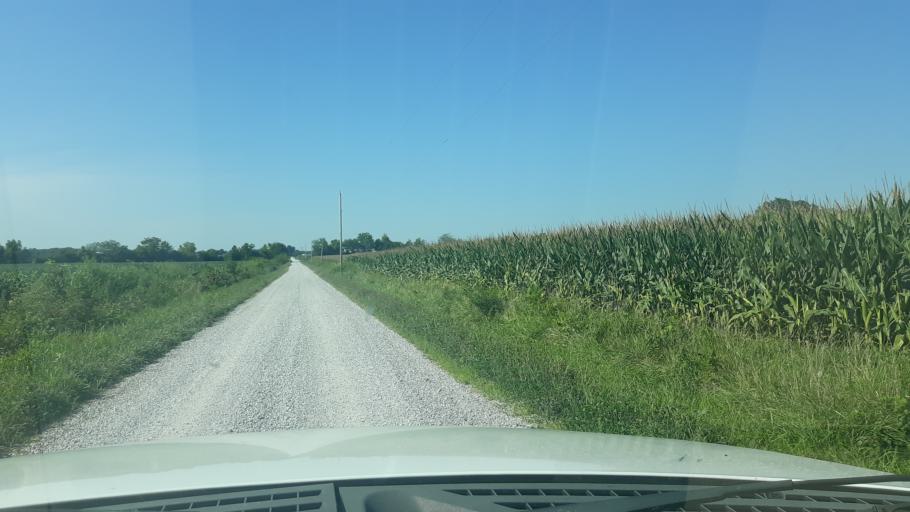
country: US
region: Illinois
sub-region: Saline County
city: Eldorado
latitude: 37.8473
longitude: -88.4849
